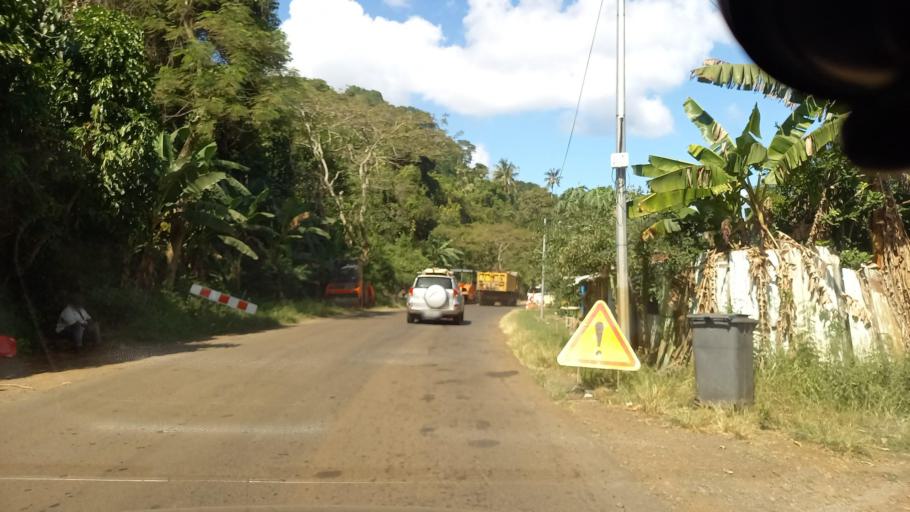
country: YT
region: M'Tsangamouji
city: M'Tsangamouji
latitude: -12.7568
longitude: 45.0896
